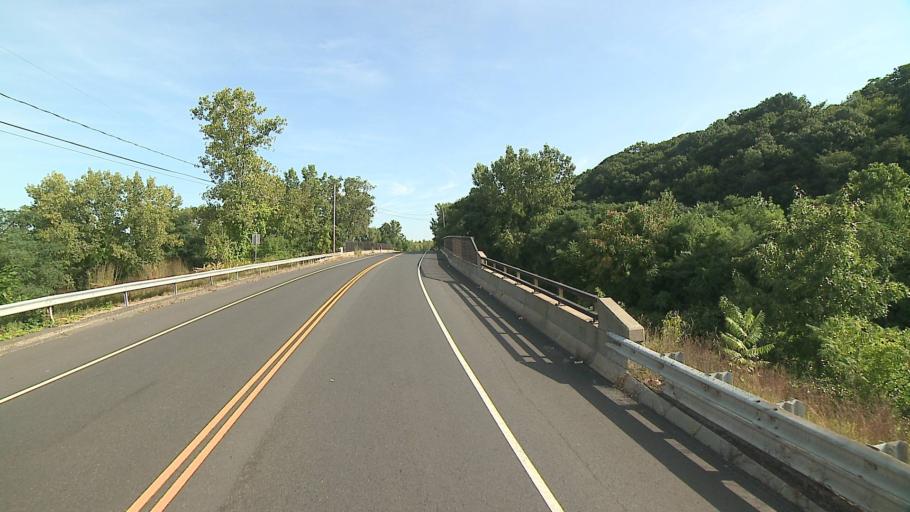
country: US
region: Connecticut
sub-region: New Haven County
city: Waterbury
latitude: 41.5664
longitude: -73.0550
